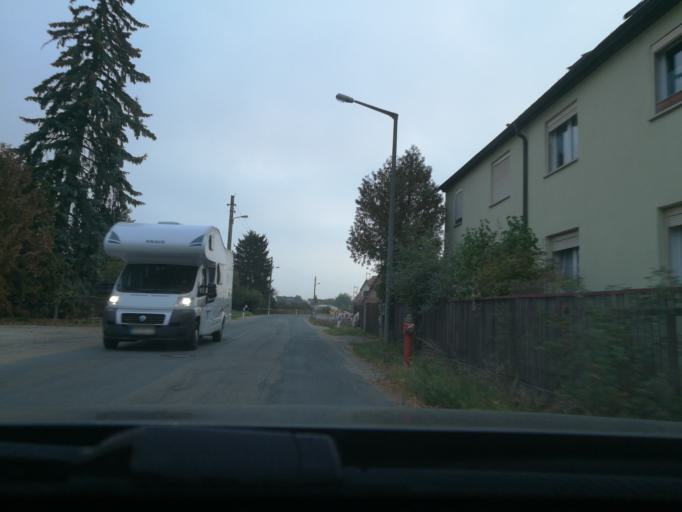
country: DE
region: Bavaria
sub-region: Regierungsbezirk Mittelfranken
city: Wetzendorf
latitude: 49.4930
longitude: 11.0406
